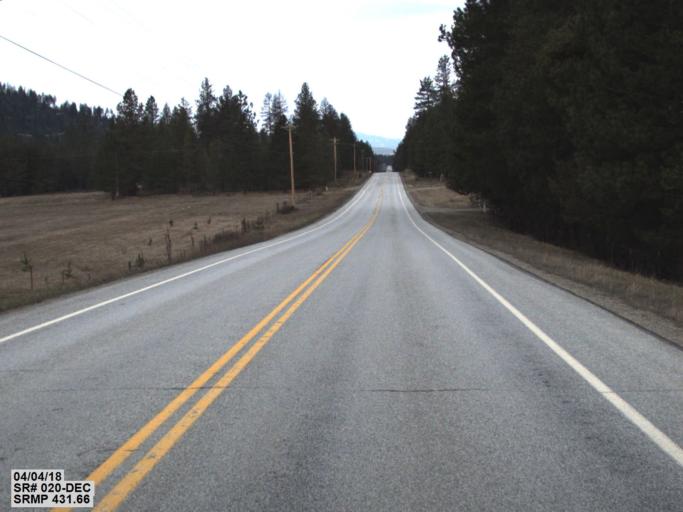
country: US
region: Washington
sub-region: Pend Oreille County
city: Newport
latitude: 48.2246
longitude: -117.1271
